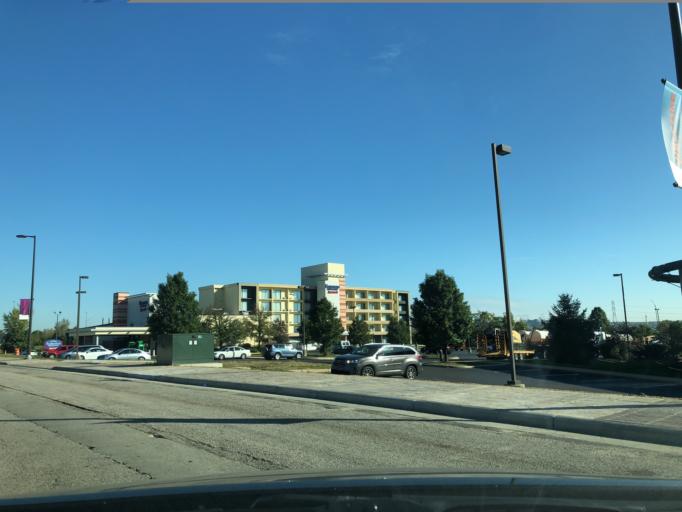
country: US
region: Ohio
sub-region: Hamilton County
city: Glendale
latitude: 39.2804
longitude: -84.4435
